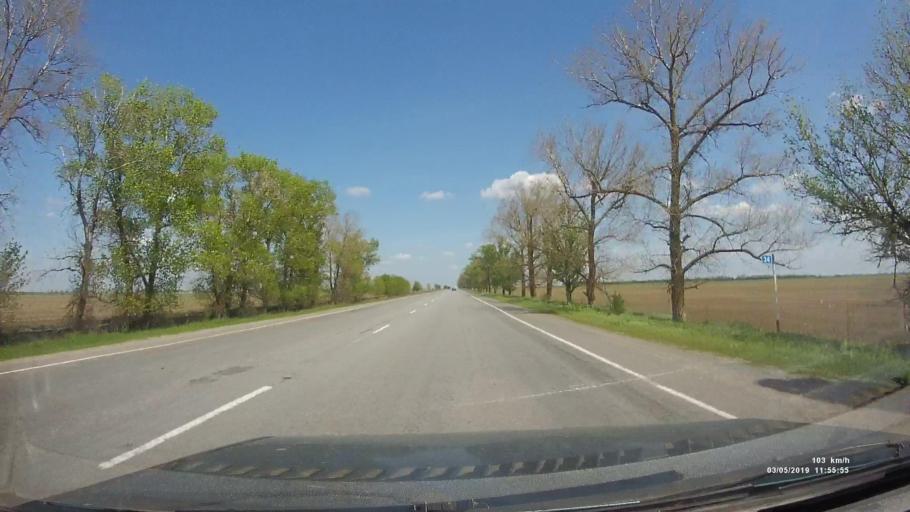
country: RU
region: Rostov
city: Bagayevskaya
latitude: 47.1873
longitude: 40.2957
